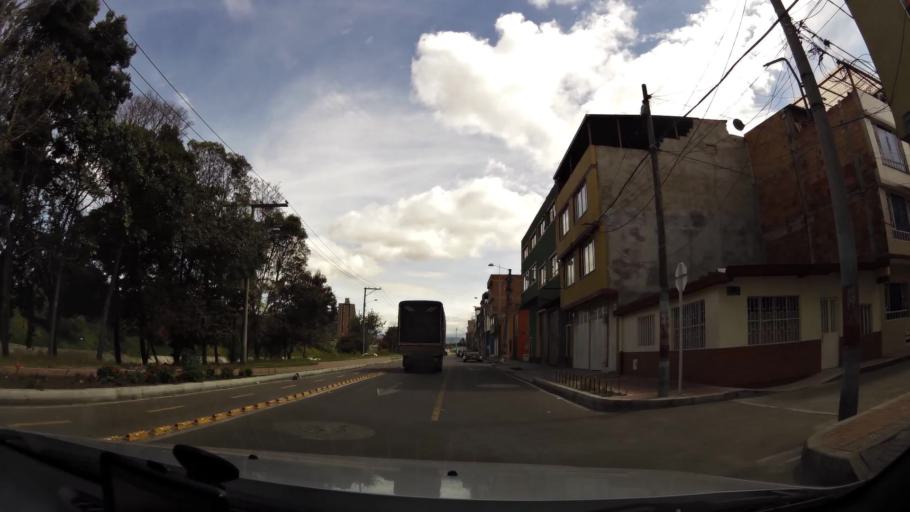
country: CO
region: Bogota D.C.
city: Bogota
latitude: 4.6283
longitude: -74.1264
